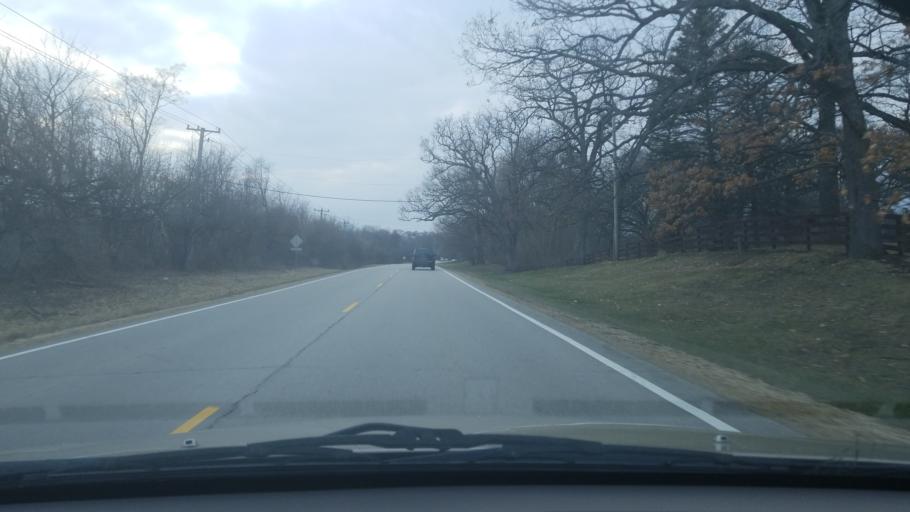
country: US
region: Illinois
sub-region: Kane County
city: Carpentersville
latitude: 42.1539
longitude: -88.2443
